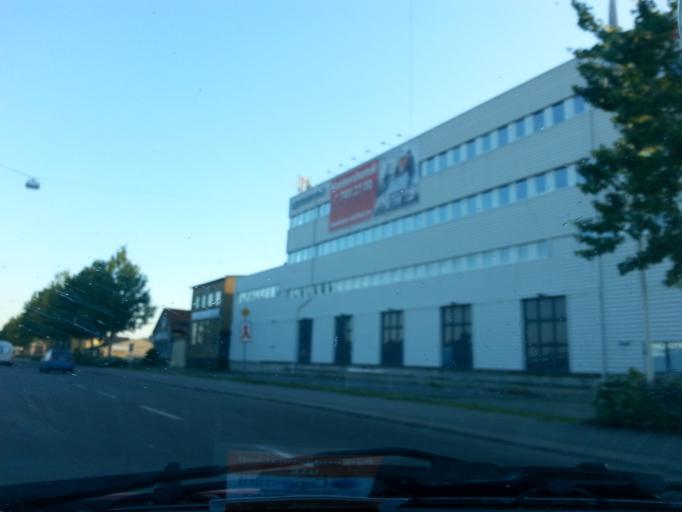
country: SE
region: Vaestra Goetaland
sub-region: Goteborg
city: Goeteborg
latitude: 57.7308
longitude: 11.9991
